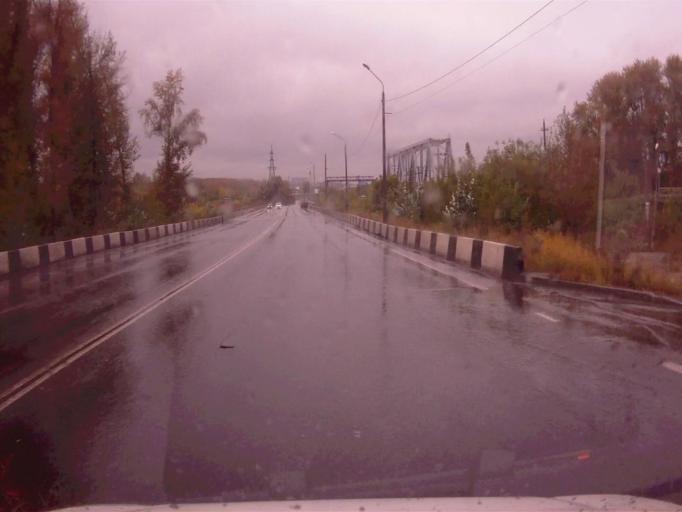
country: RU
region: Chelyabinsk
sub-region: Gorod Chelyabinsk
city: Chelyabinsk
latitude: 55.1987
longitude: 61.4047
